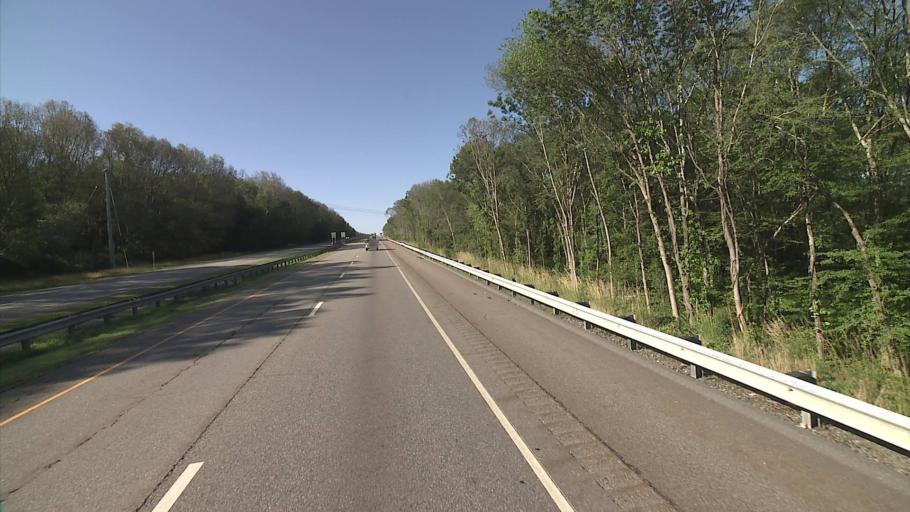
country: US
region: Connecticut
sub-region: Windham County
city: Plainfield Village
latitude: 41.6424
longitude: -71.9355
